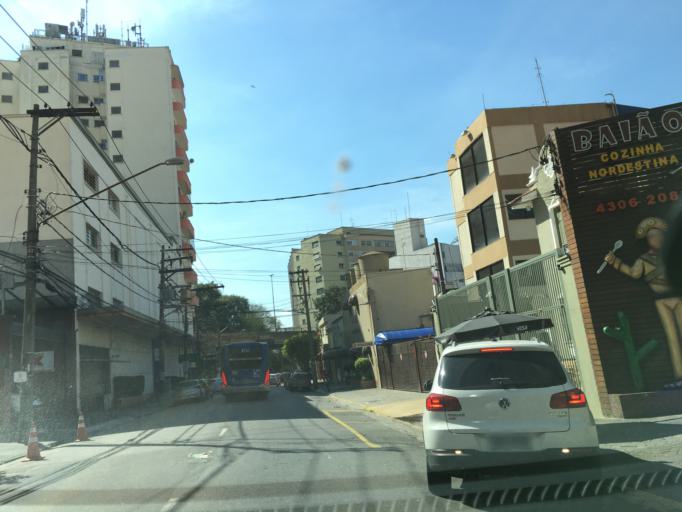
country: BR
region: Sao Paulo
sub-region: Sao Paulo
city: Sao Paulo
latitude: -23.5331
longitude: -46.6626
